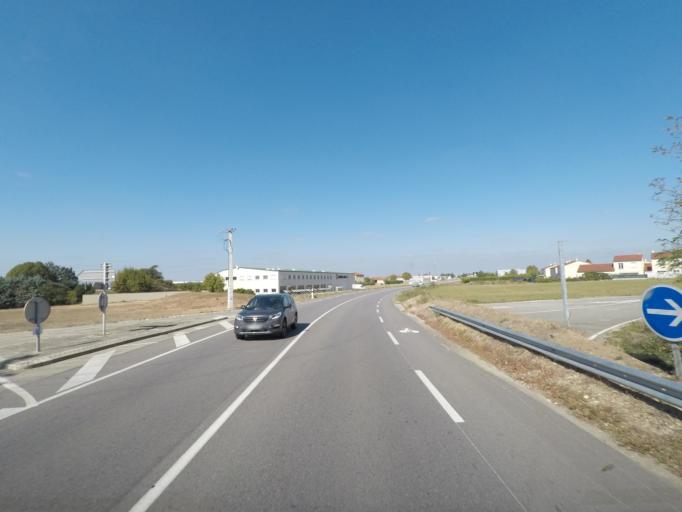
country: FR
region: Rhone-Alpes
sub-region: Departement de la Drome
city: Chabeuil
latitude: 44.8975
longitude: 5.0093
